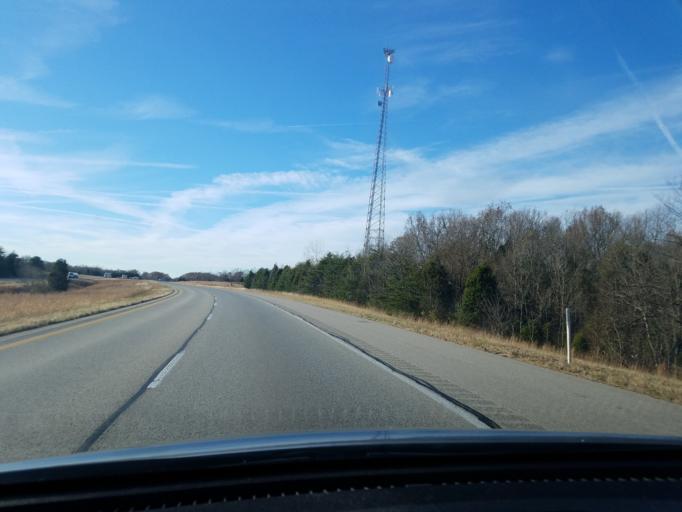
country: US
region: Indiana
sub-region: Harrison County
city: Corydon
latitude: 38.2492
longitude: -86.2666
